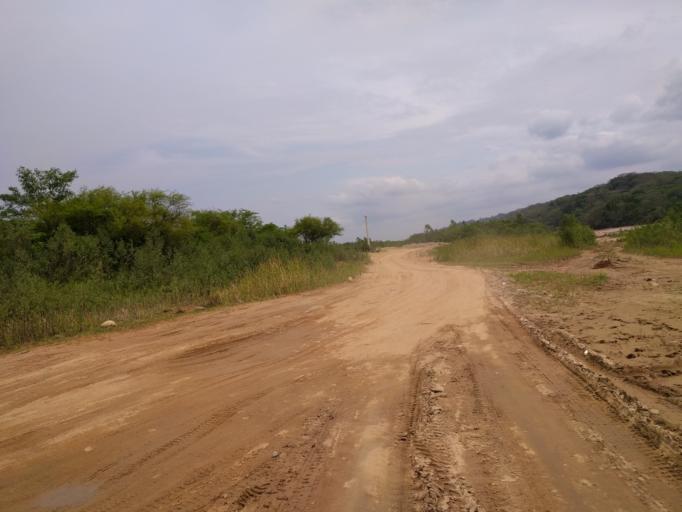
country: BO
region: Santa Cruz
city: Santa Rita
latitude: -17.9379
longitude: -63.3629
